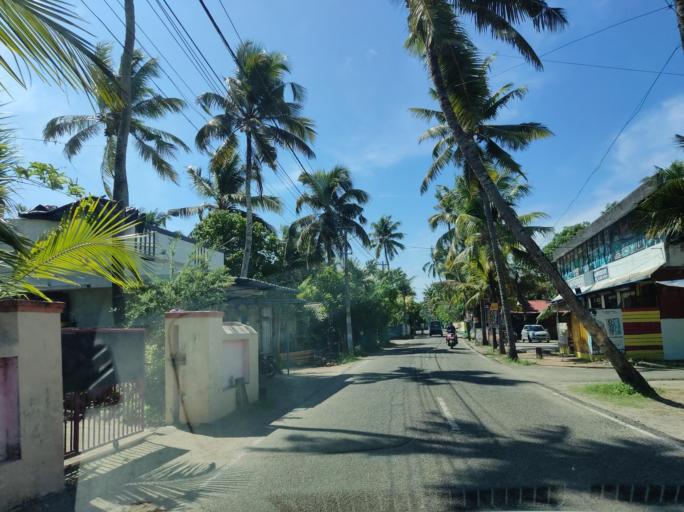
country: IN
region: Kerala
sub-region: Alappuzha
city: Kayankulam
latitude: 9.2268
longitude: 76.4223
